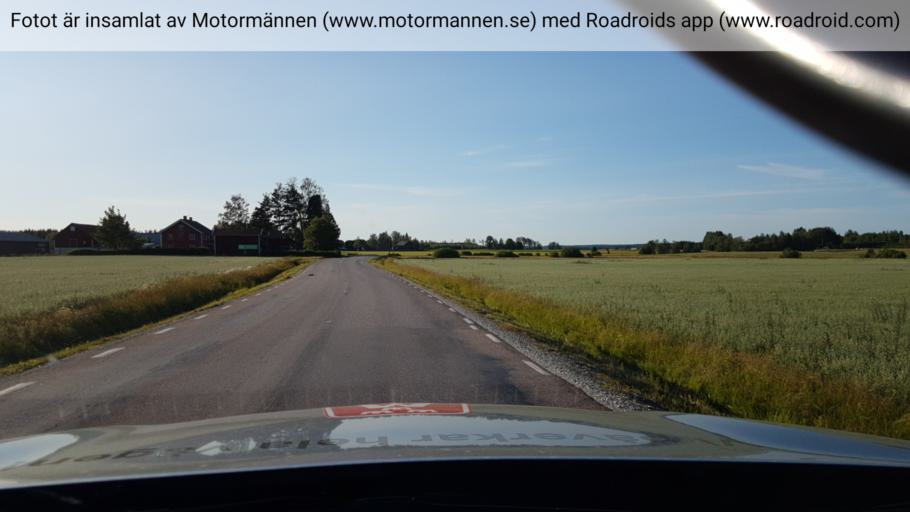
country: SE
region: Vaestmanland
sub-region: Surahammars Kommun
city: Ramnas
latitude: 59.9136
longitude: 16.3210
